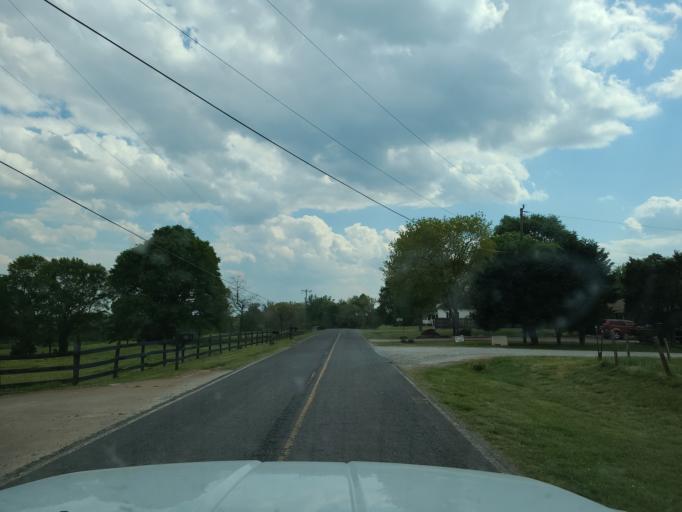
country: US
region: North Carolina
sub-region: Cleveland County
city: Shelby
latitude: 35.3429
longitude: -81.5819
